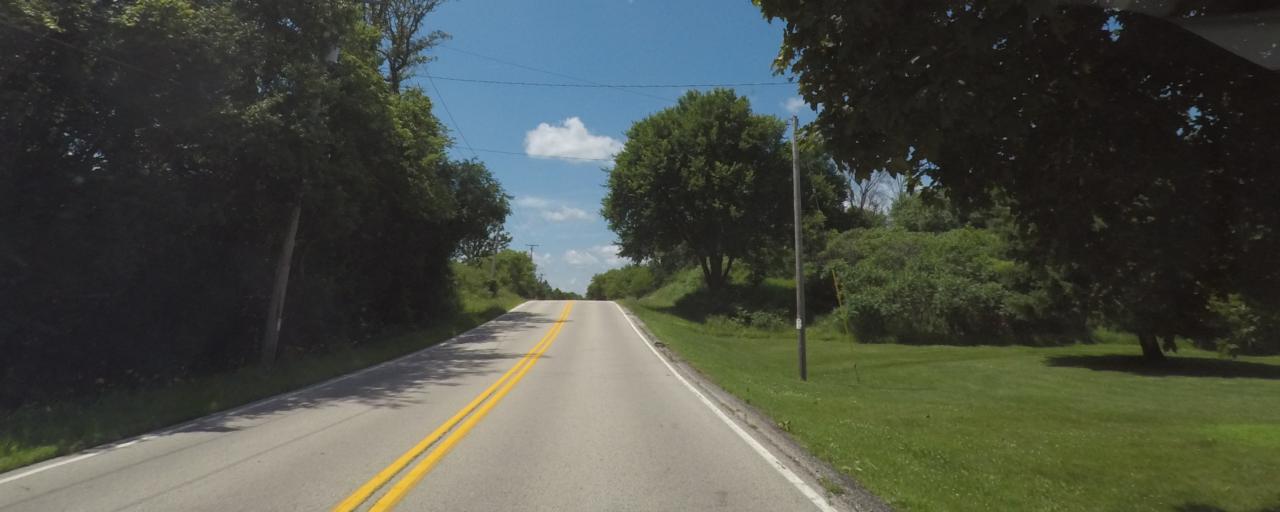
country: US
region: Wisconsin
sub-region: Waukesha County
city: Wales
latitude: 42.9953
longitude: -88.3876
